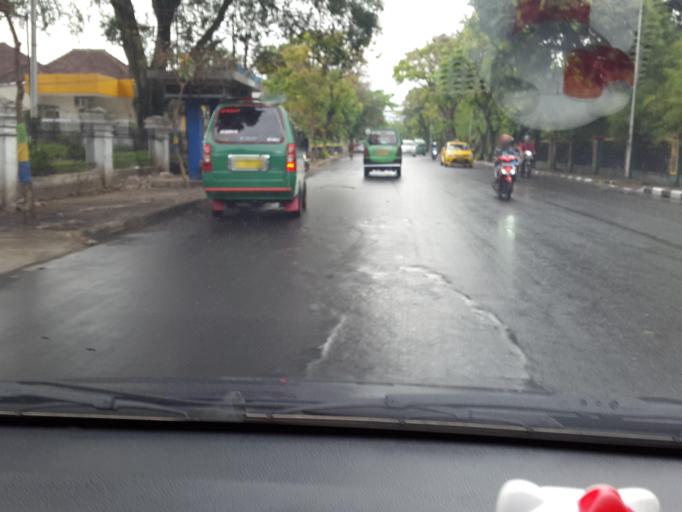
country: ID
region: West Java
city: Bandung
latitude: -6.9063
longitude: 107.6303
